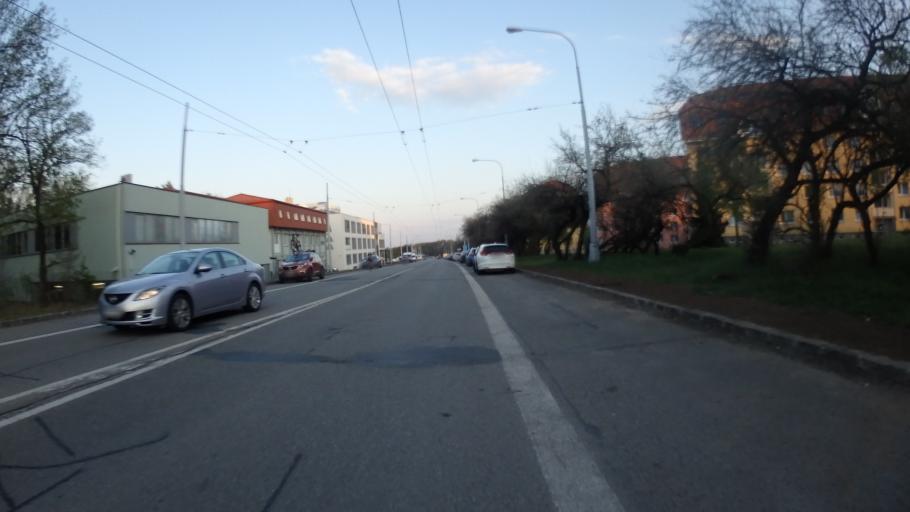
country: CZ
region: South Moravian
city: Troubsko
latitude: 49.1894
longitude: 16.5314
